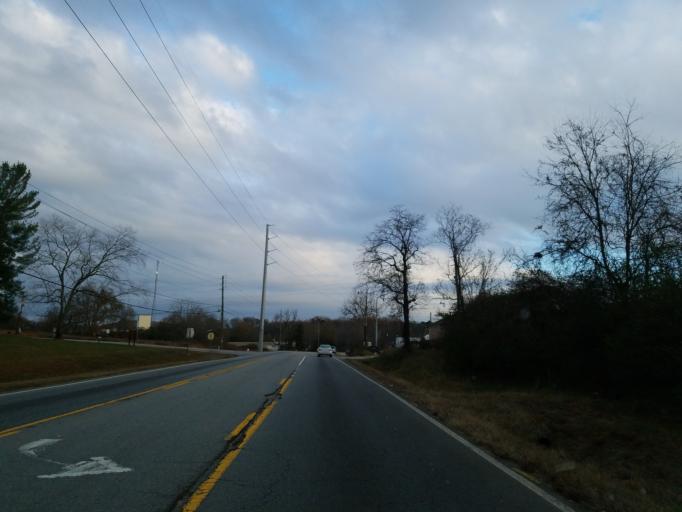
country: US
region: Georgia
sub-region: Forsyth County
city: Cumming
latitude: 34.2709
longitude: -84.0981
